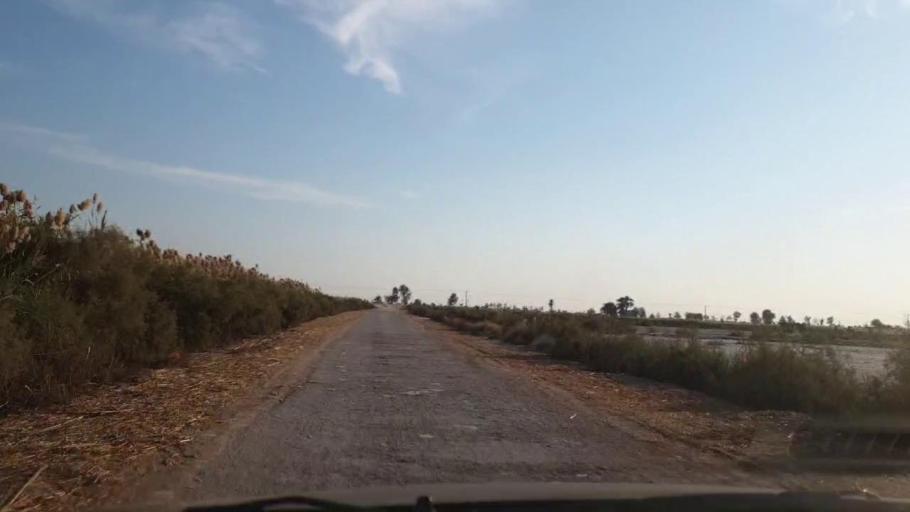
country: PK
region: Sindh
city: Khadro
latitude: 26.1800
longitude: 68.7501
